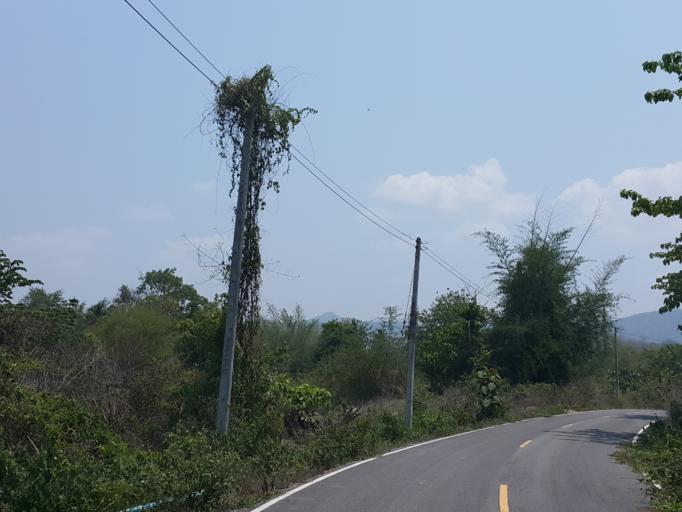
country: TH
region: Kanchanaburi
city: Sai Yok
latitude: 14.1845
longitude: 98.9583
